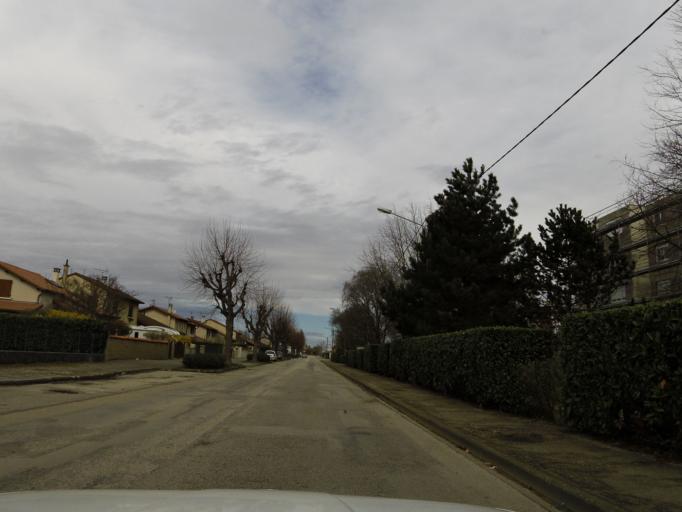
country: FR
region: Rhone-Alpes
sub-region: Departement de l'Ain
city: Amberieu-en-Bugey
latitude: 45.9612
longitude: 5.3354
